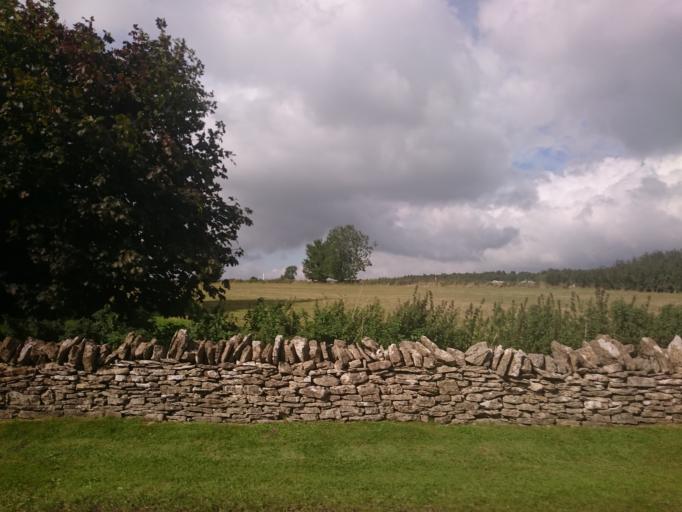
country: GB
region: England
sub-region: Gloucestershire
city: Charlton Kings
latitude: 51.8146
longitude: -2.0502
